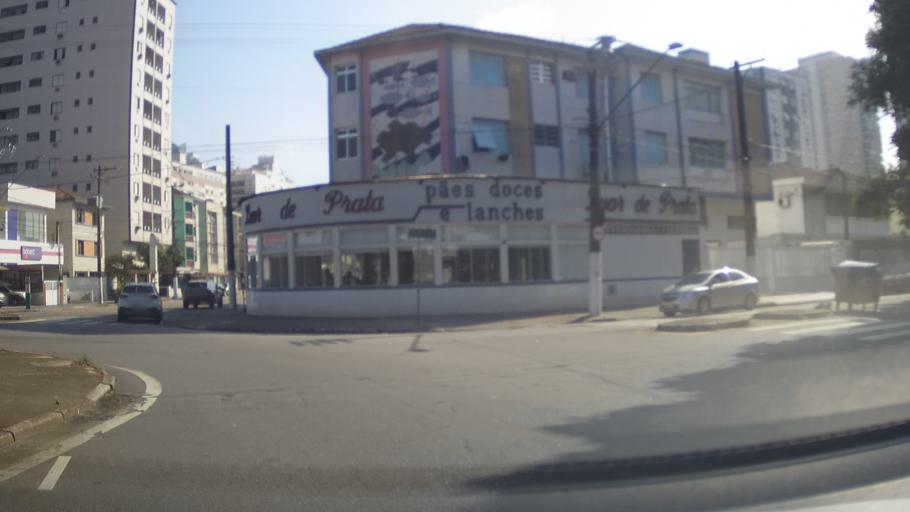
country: BR
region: Sao Paulo
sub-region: Santos
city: Santos
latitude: -23.9869
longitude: -46.3030
